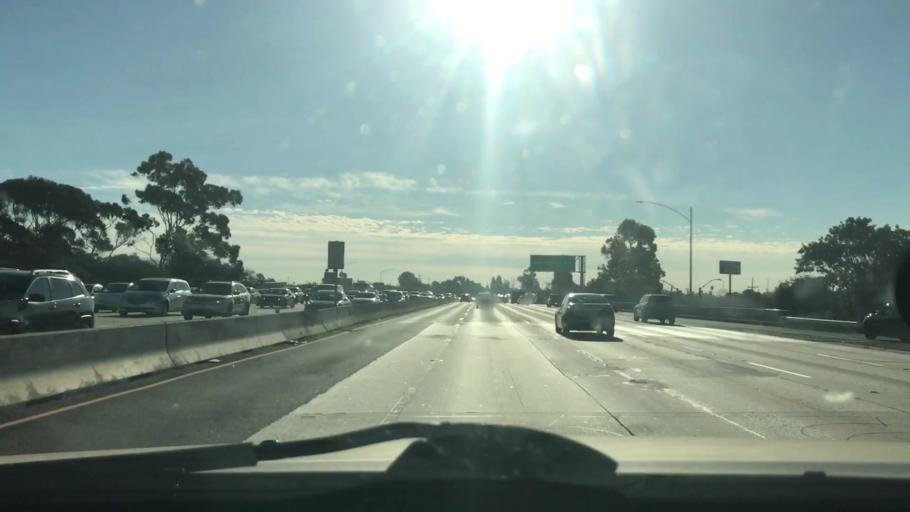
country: US
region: California
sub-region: Los Angeles County
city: Lawndale
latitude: 33.8850
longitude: -118.3532
